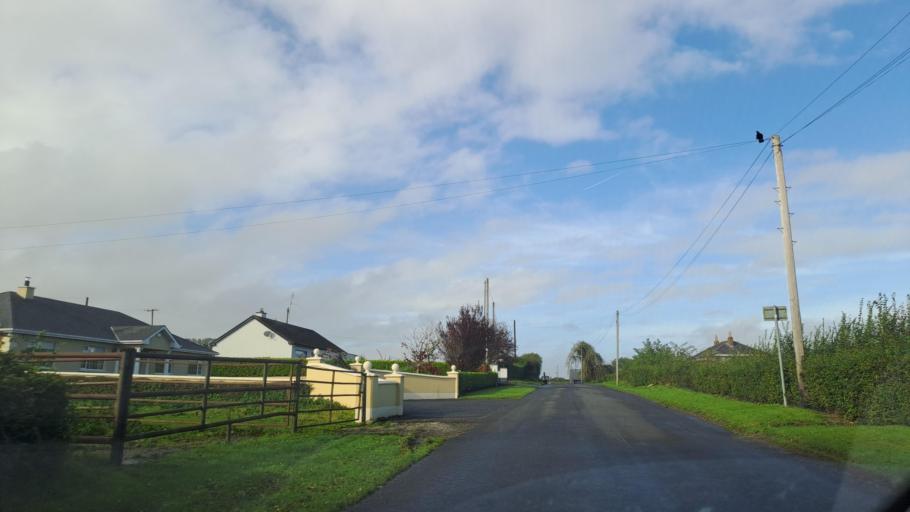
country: IE
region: Ulster
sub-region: County Monaghan
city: Carrickmacross
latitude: 53.8673
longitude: -6.6614
